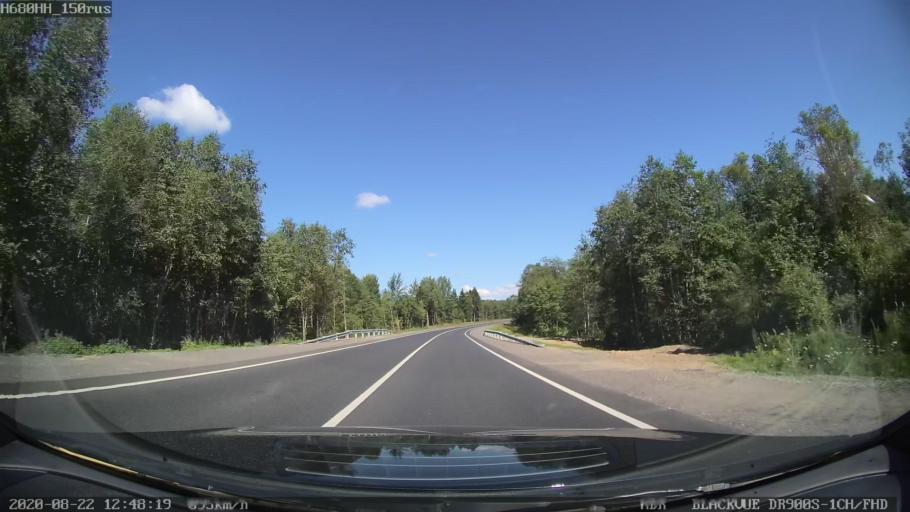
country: RU
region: Tverskaya
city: Rameshki
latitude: 57.4381
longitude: 36.1832
